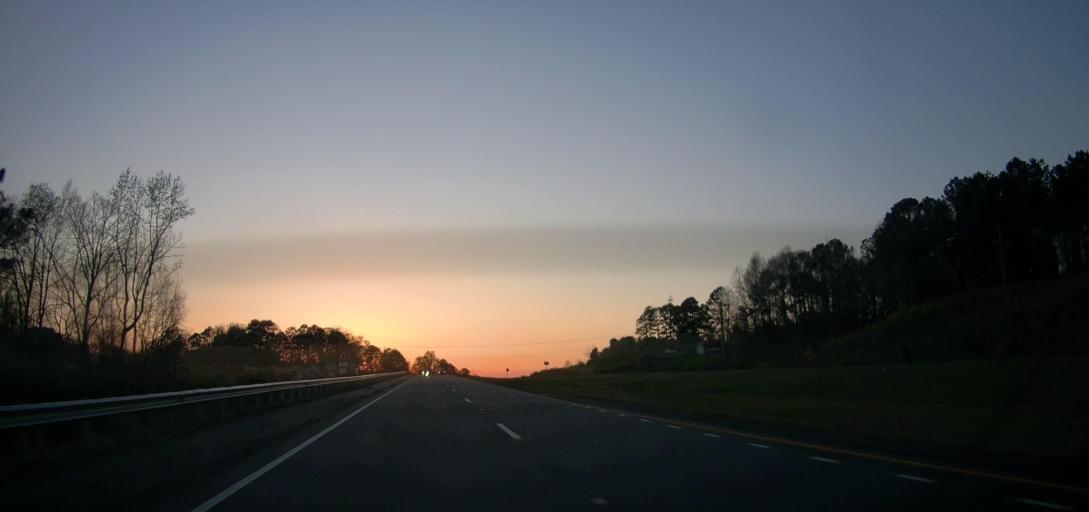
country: US
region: Alabama
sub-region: Tallapoosa County
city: Dadeville
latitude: 32.8807
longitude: -85.8480
